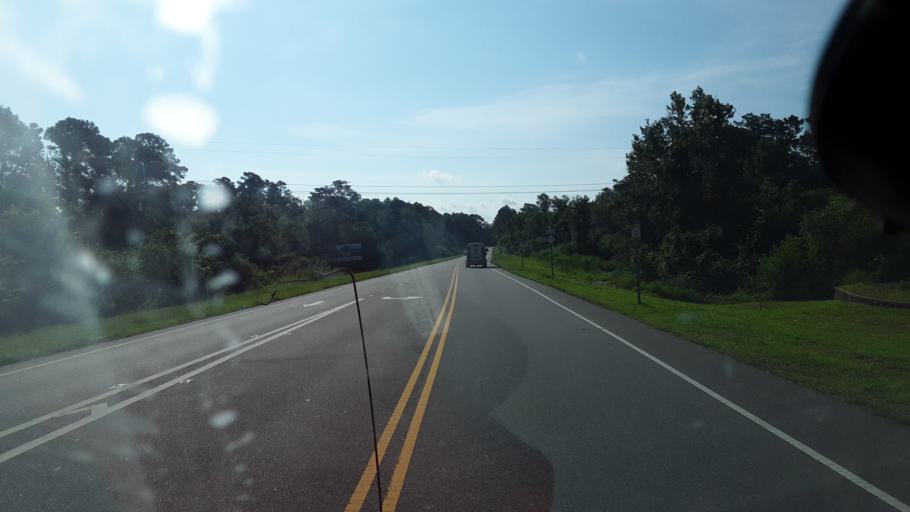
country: US
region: North Carolina
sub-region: Brunswick County
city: Belville
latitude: 34.2300
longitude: -77.9909
